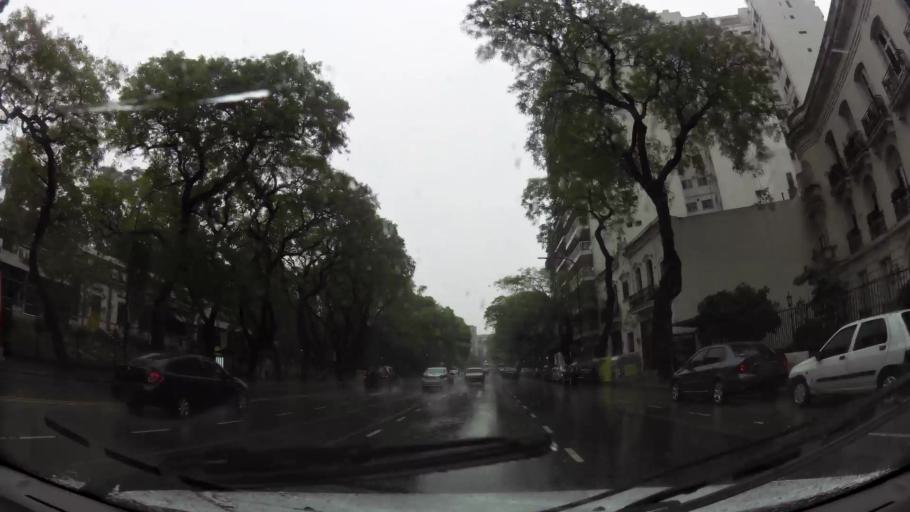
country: AR
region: Buenos Aires F.D.
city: Retiro
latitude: -34.5817
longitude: -58.4159
